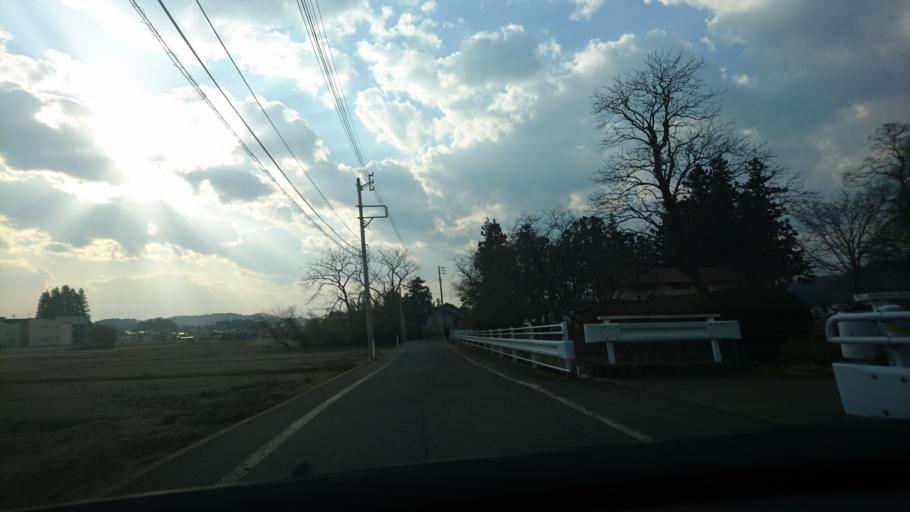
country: JP
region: Iwate
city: Ichinoseki
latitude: 38.9366
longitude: 141.0983
